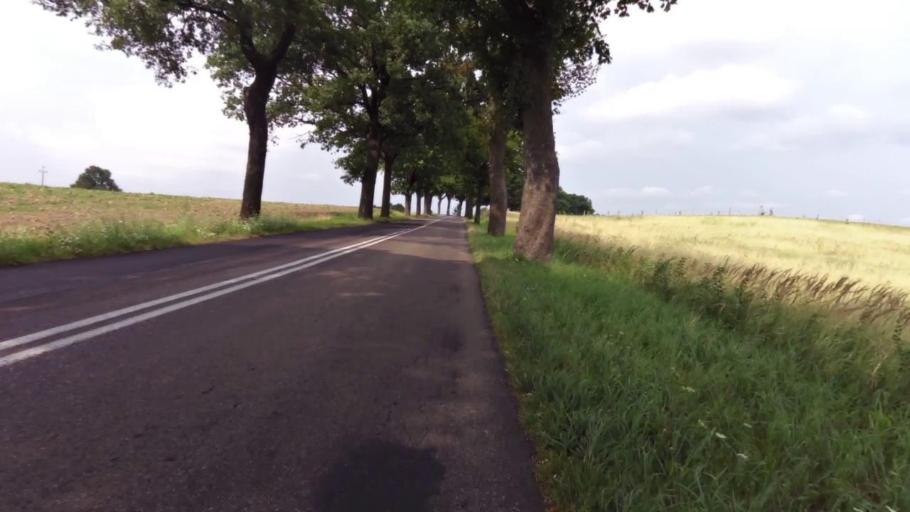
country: PL
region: West Pomeranian Voivodeship
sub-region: Powiat drawski
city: Drawsko Pomorskie
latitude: 53.5603
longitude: 15.8286
